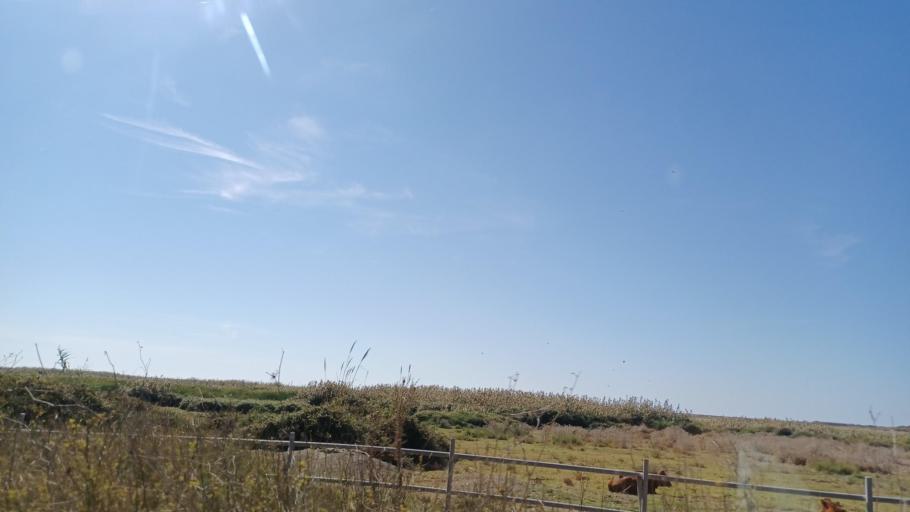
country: CY
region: Larnaka
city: Kolossi
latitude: 34.6355
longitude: 32.9258
